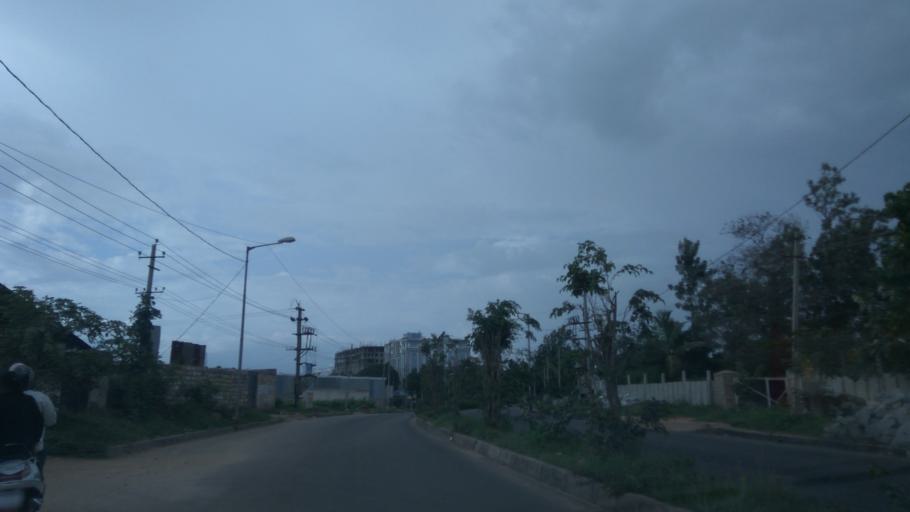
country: IN
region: Karnataka
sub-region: Bangalore Urban
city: Yelahanka
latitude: 13.1105
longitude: 77.6337
